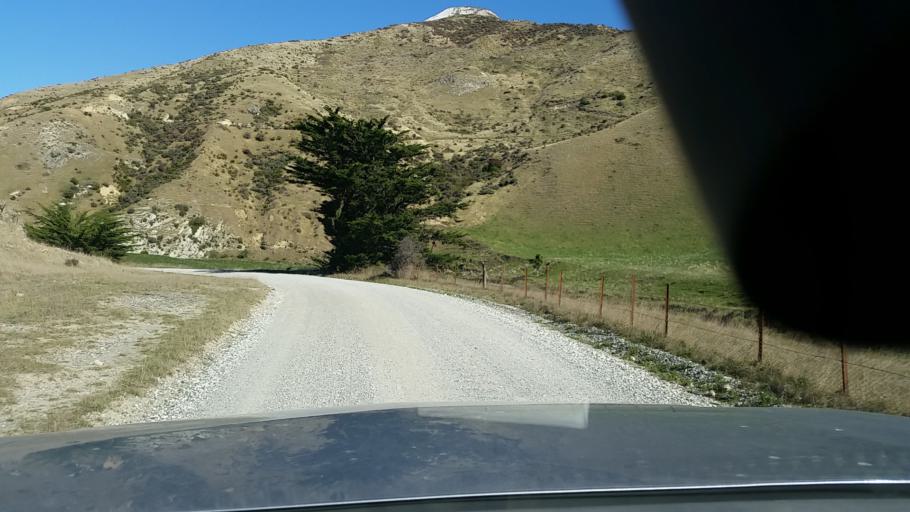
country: NZ
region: Marlborough
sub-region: Marlborough District
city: Blenheim
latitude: -41.8414
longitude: 174.1809
